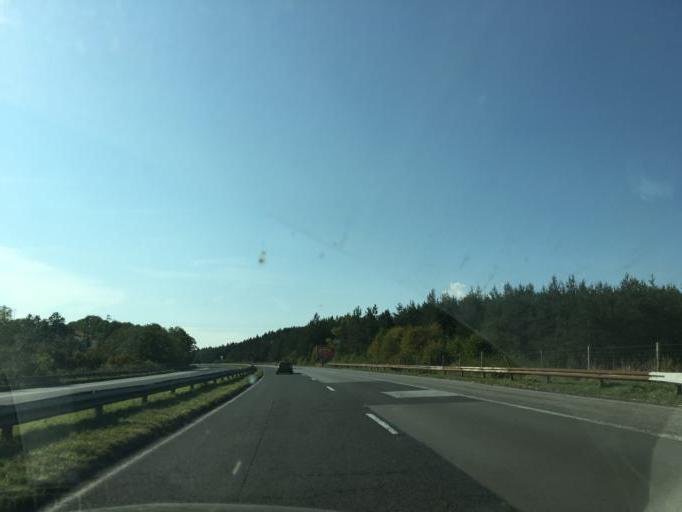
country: BG
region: Sofiya
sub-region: Obshtina Ikhtiman
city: Ikhtiman
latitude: 42.3794
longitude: 23.8771
